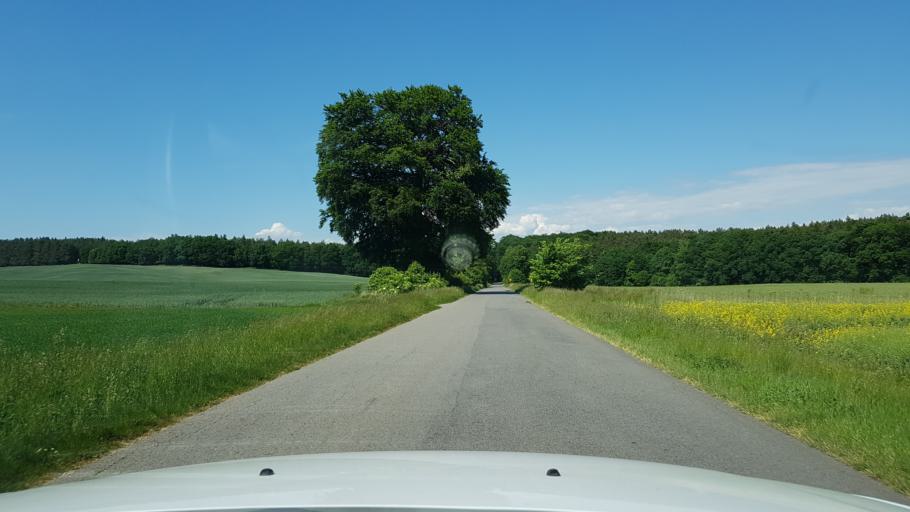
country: PL
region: West Pomeranian Voivodeship
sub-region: Powiat gryfinski
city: Banie
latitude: 53.0497
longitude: 14.6263
